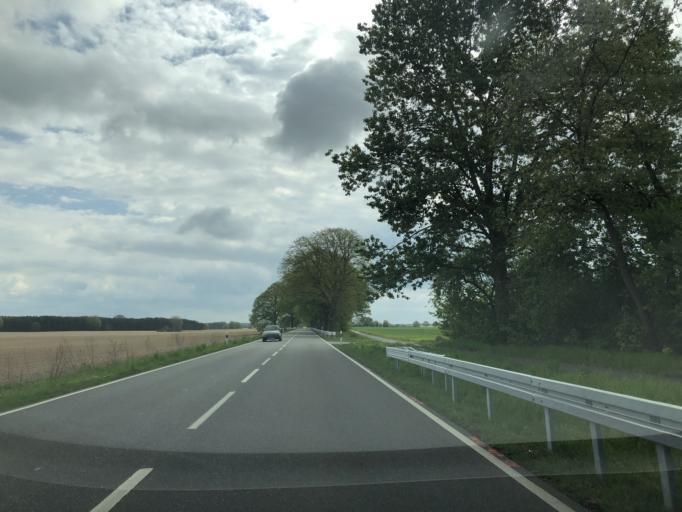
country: DE
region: Mecklenburg-Vorpommern
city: Lubz
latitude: 53.4638
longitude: 12.1396
